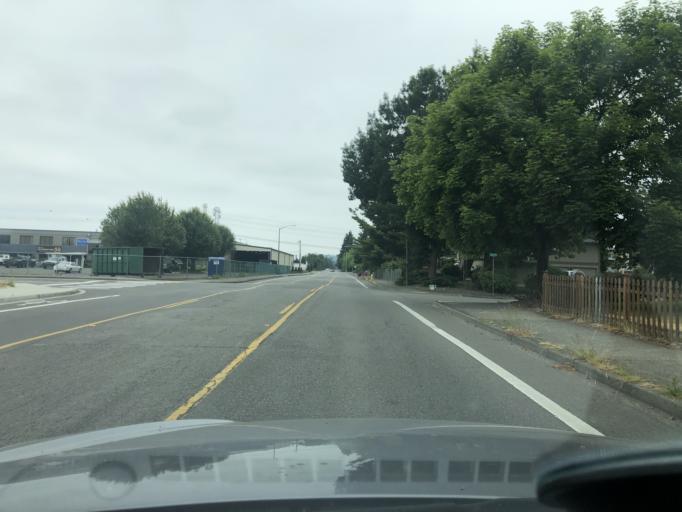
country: US
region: Washington
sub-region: King County
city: Auburn
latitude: 47.3335
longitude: -122.2192
